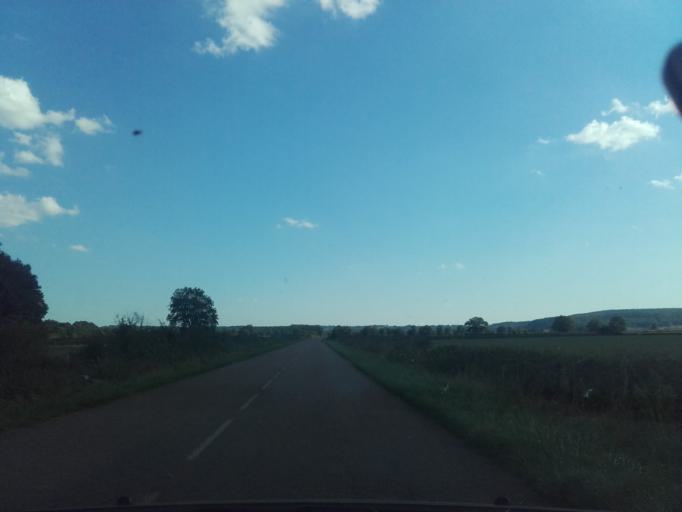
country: FR
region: Bourgogne
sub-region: Departement de Saone-et-Loire
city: Epinac
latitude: 47.0019
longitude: 4.4769
